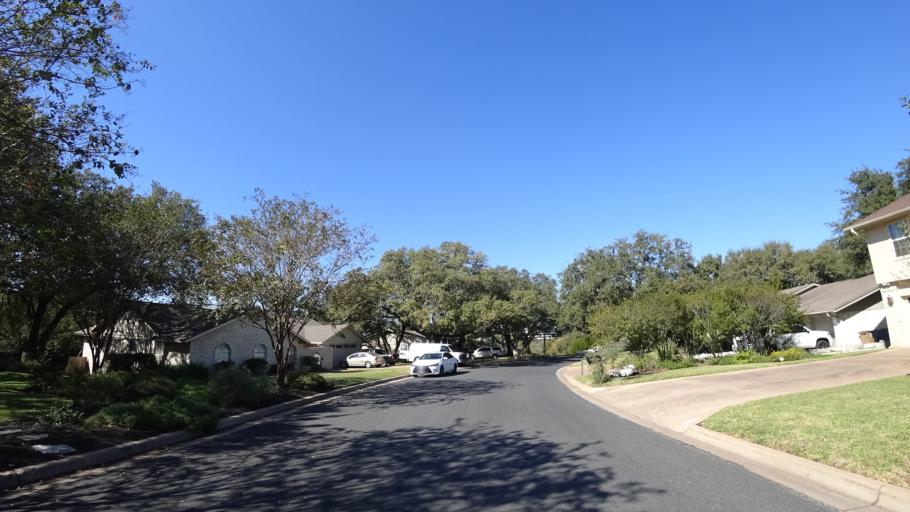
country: US
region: Texas
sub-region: Williamson County
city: Jollyville
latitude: 30.3860
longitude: -97.7489
